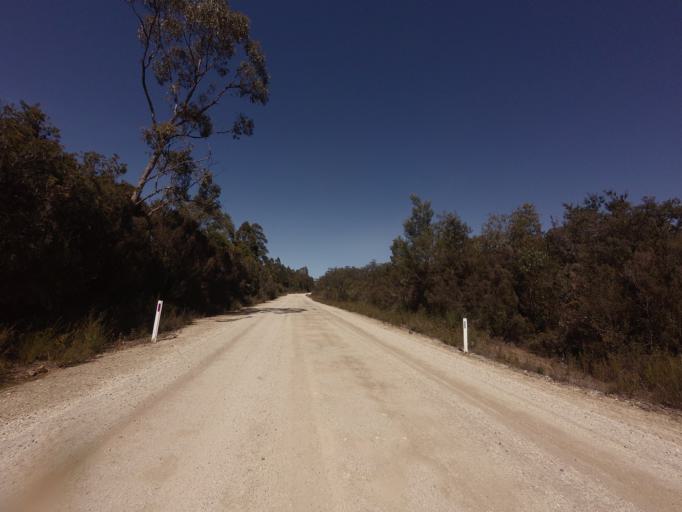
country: AU
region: Tasmania
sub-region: Huon Valley
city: Geeveston
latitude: -42.9004
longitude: 146.3734
